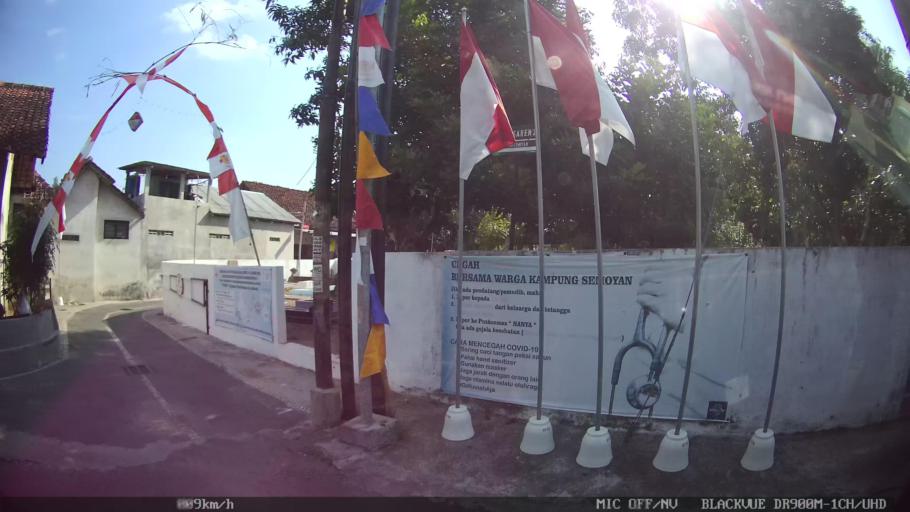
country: ID
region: Daerah Istimewa Yogyakarta
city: Sewon
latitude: -7.8343
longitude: 110.3962
